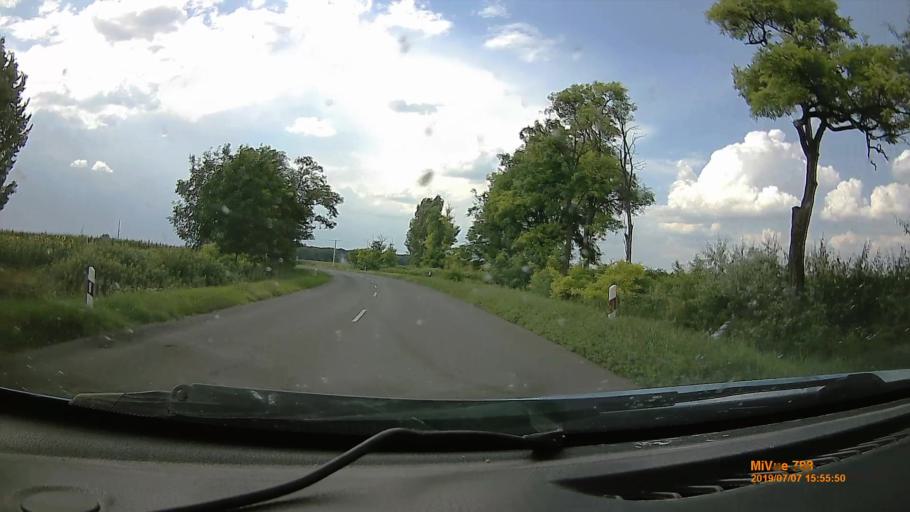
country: HU
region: Pest
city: Szentlorinckata
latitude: 47.5624
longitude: 19.7827
